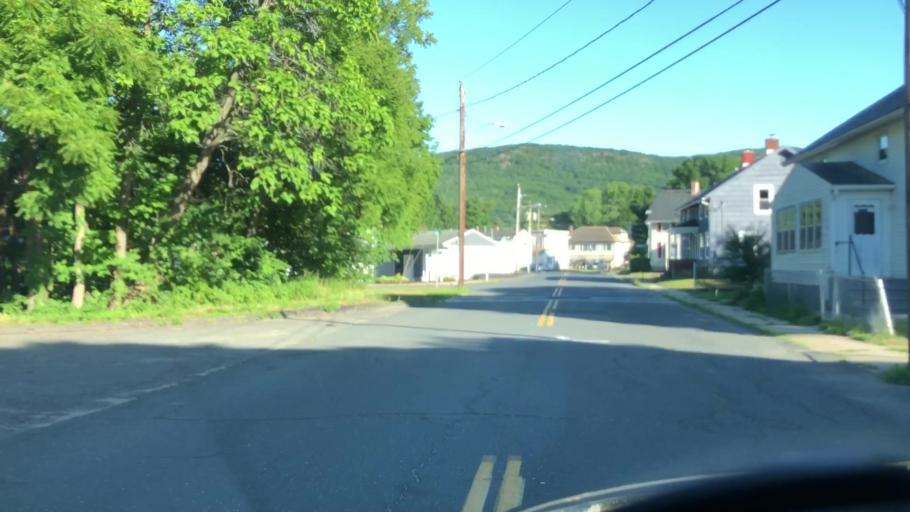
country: US
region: Massachusetts
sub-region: Hampshire County
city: Easthampton
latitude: 42.2729
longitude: -72.6542
